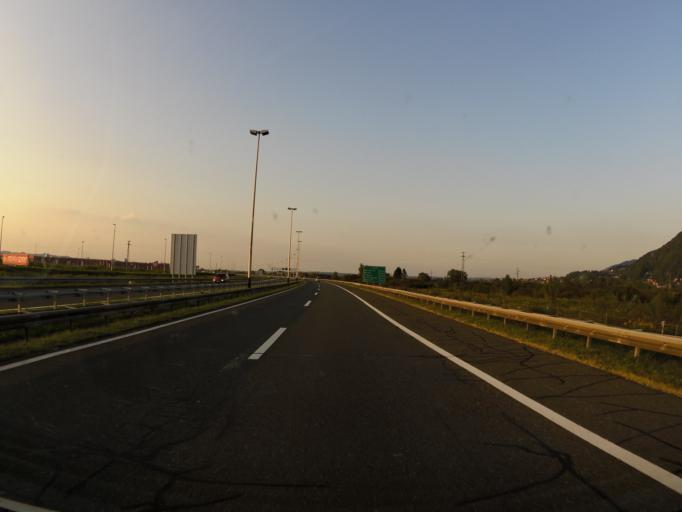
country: HR
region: Zagrebacka
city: Zapresic
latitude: 45.8600
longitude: 15.8307
